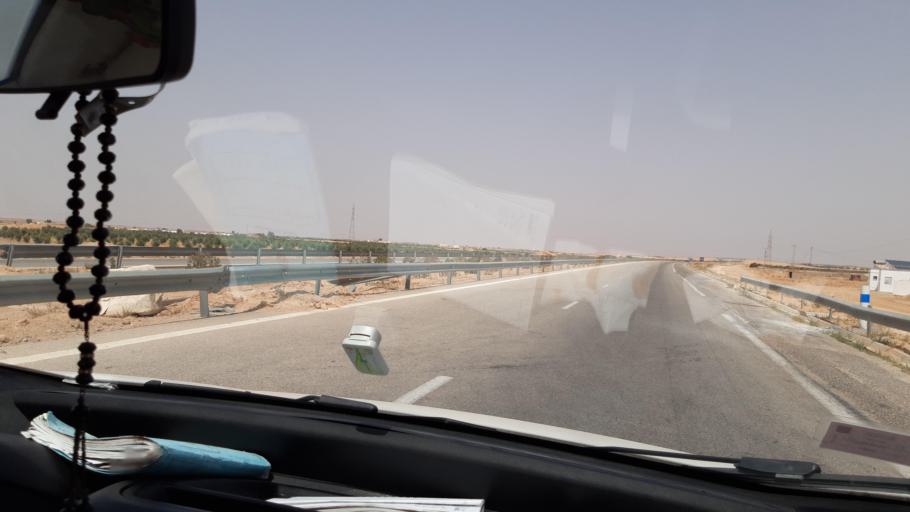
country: TN
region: Safaqis
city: Skhira
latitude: 34.3386
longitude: 10.0091
